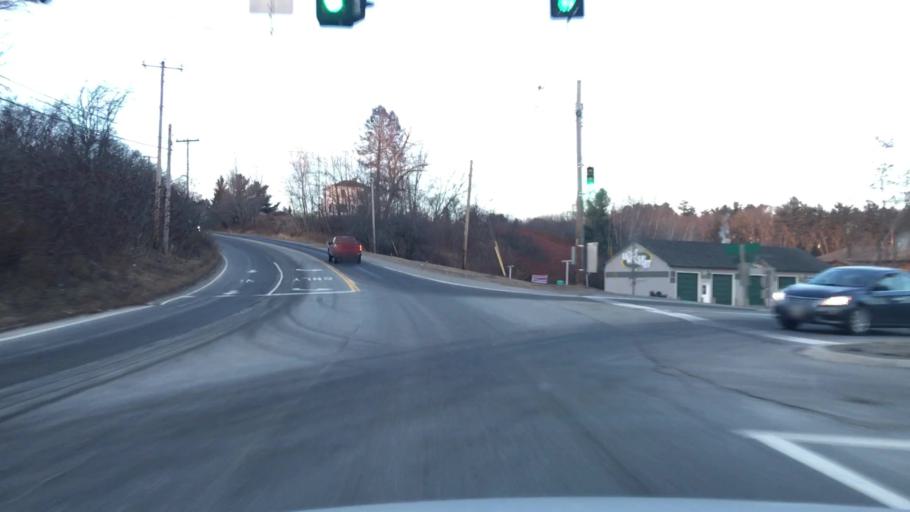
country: US
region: Maine
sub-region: Penobscot County
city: Brewer
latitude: 44.8146
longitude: -68.7382
